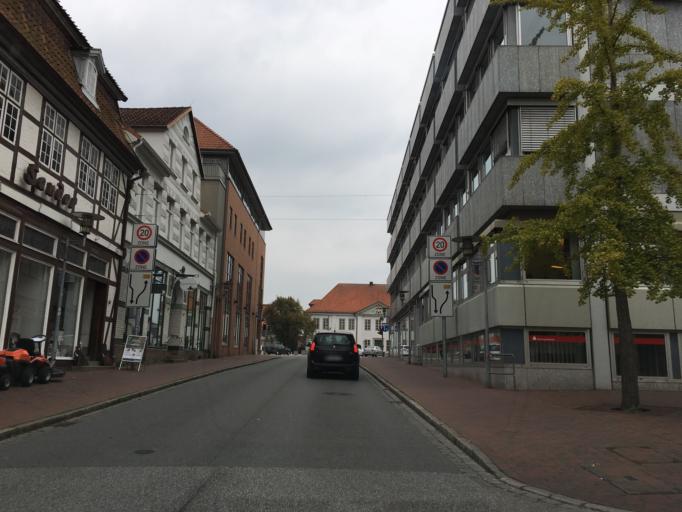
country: DE
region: Schleswig-Holstein
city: Ratzeburg
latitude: 53.6992
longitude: 10.7757
